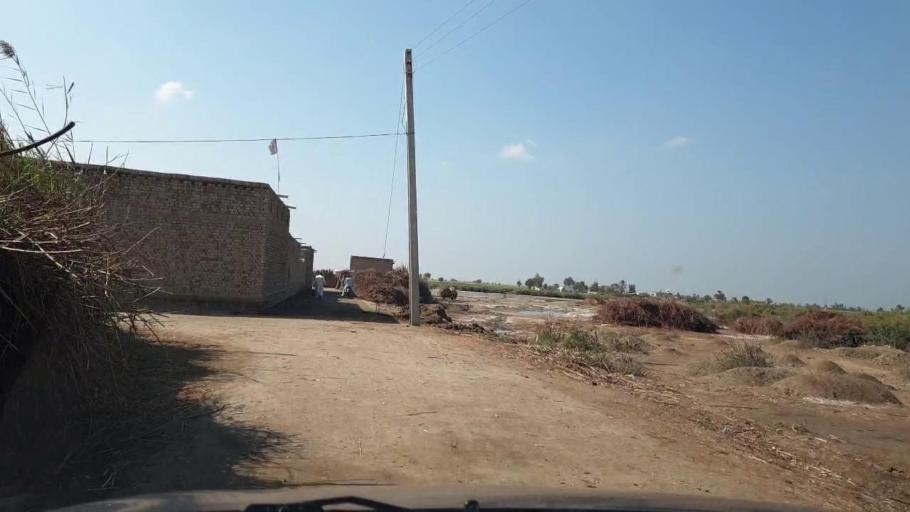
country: PK
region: Sindh
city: Khadro
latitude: 26.0785
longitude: 68.7433
